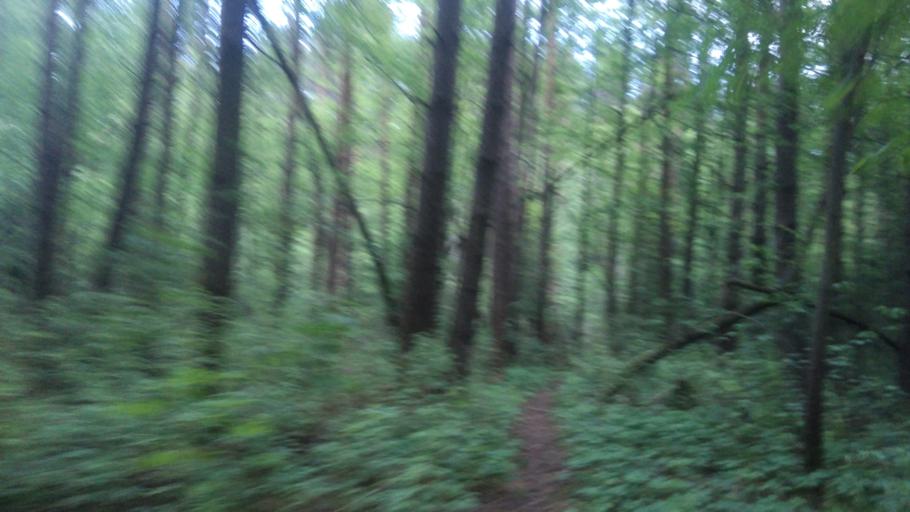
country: RU
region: Perm
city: Froly
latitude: 57.9619
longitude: 56.3005
